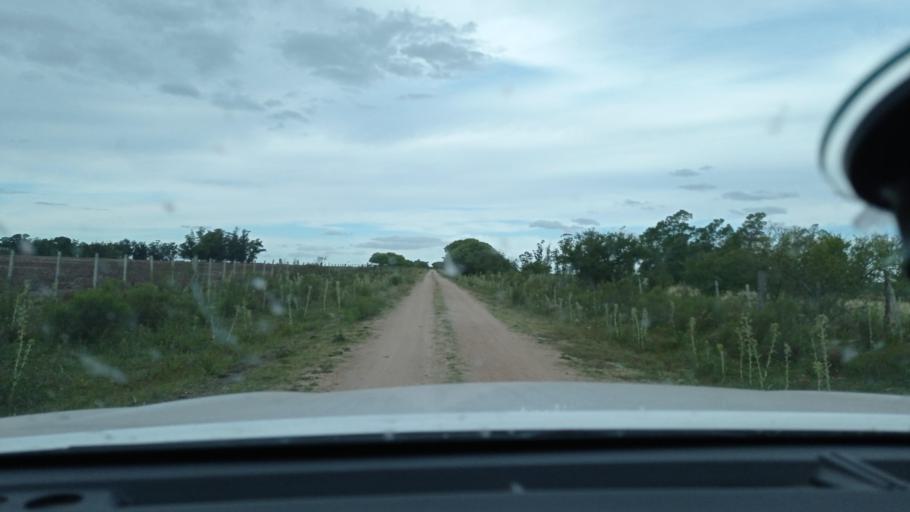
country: UY
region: Florida
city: Casupa
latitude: -34.1180
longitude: -55.8230
